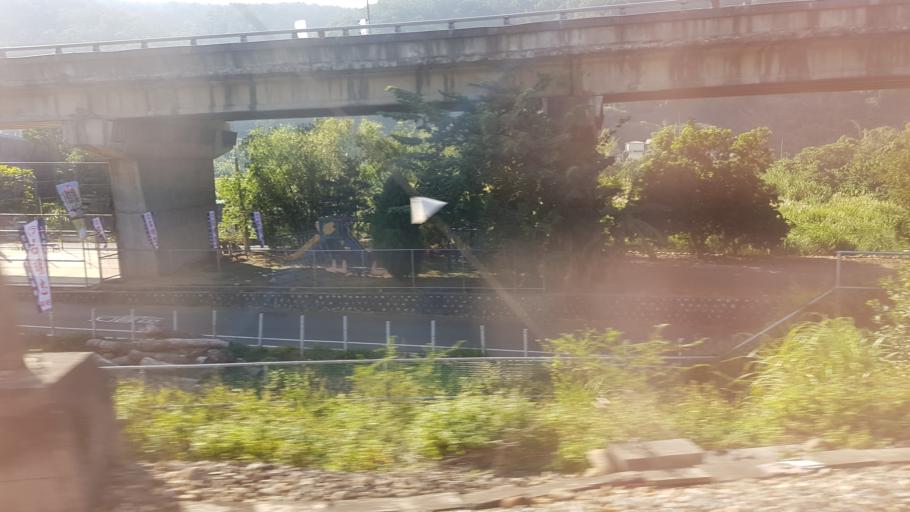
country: TW
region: Taiwan
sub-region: Miaoli
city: Miaoli
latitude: 24.4237
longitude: 120.7743
